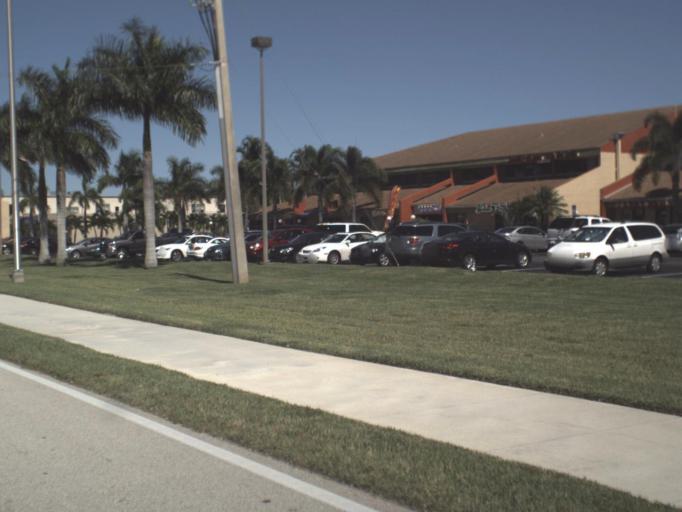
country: US
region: Florida
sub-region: Lee County
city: Villas
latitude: 26.5533
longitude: -81.8716
